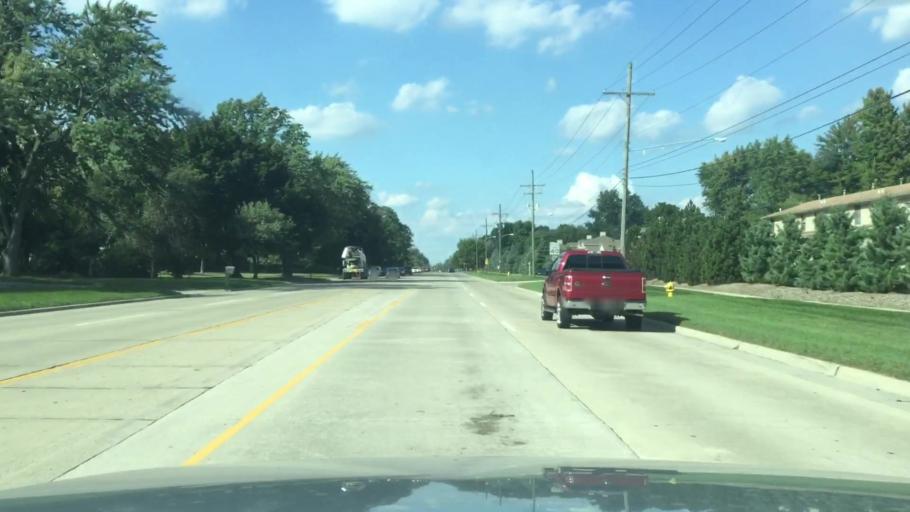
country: US
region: Michigan
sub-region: Wayne County
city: Westland
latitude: 42.3266
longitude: -83.4087
